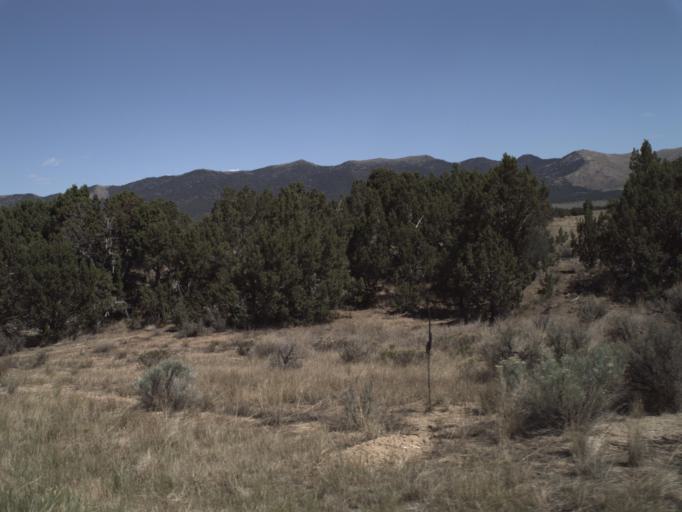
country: US
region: Utah
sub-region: Utah County
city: Genola
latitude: 39.9344
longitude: -112.1742
